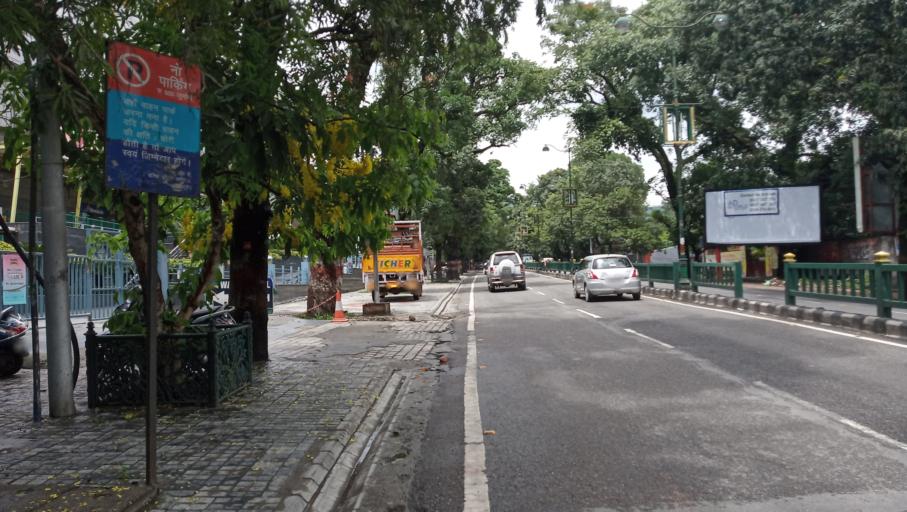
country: IN
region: Uttarakhand
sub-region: Dehradun
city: Dehradun
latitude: 30.3655
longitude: 78.0707
